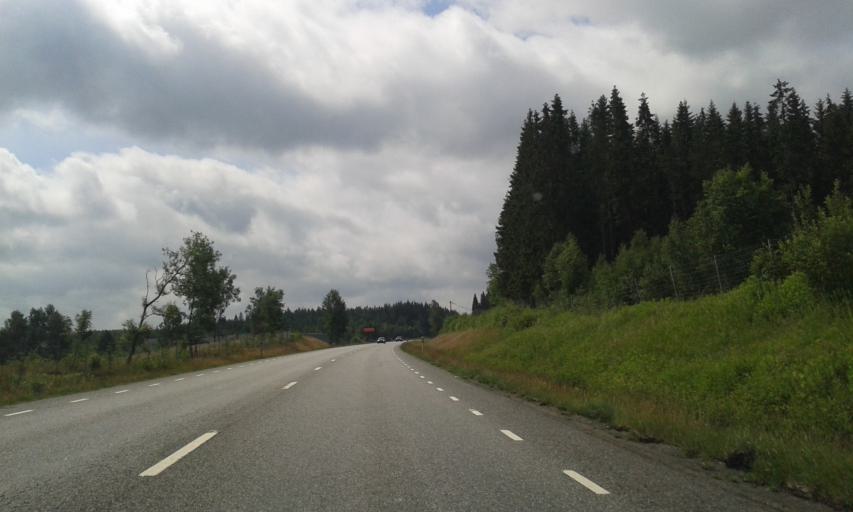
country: SE
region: Vaestra Goetaland
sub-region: Tranemo Kommun
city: Limmared
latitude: 57.5194
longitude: 13.3420
